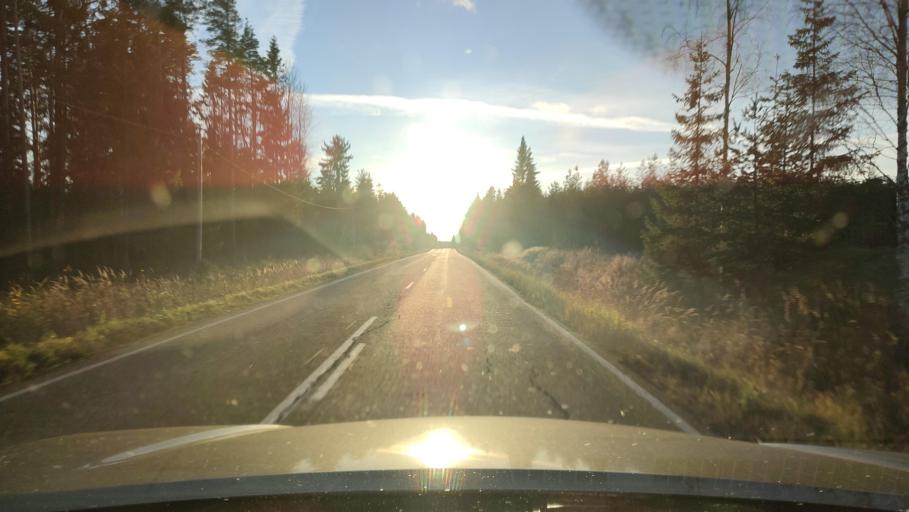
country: FI
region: Ostrobothnia
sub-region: Vaasa
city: Malax
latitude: 62.6970
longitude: 21.5723
